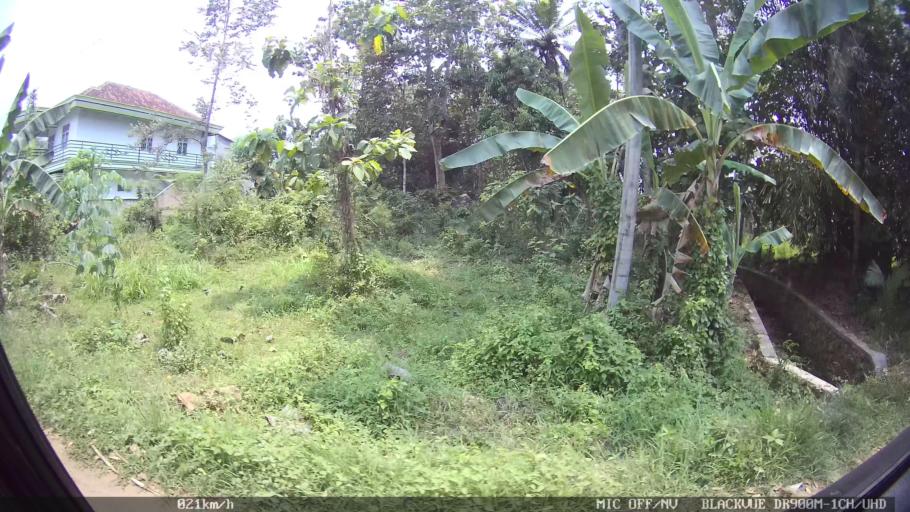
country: ID
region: Lampung
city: Pringsewu
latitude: -5.3829
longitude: 105.0137
